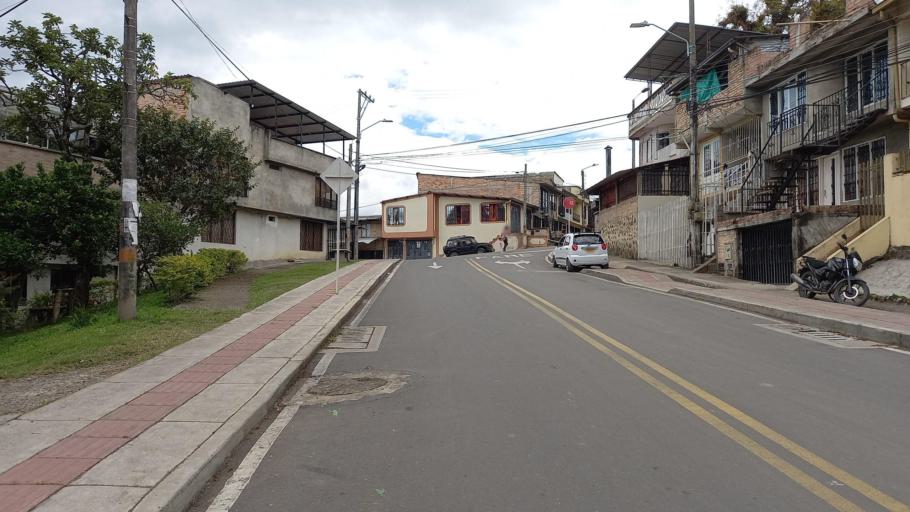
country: CO
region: Cauca
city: Popayan
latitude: 2.4595
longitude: -76.6435
